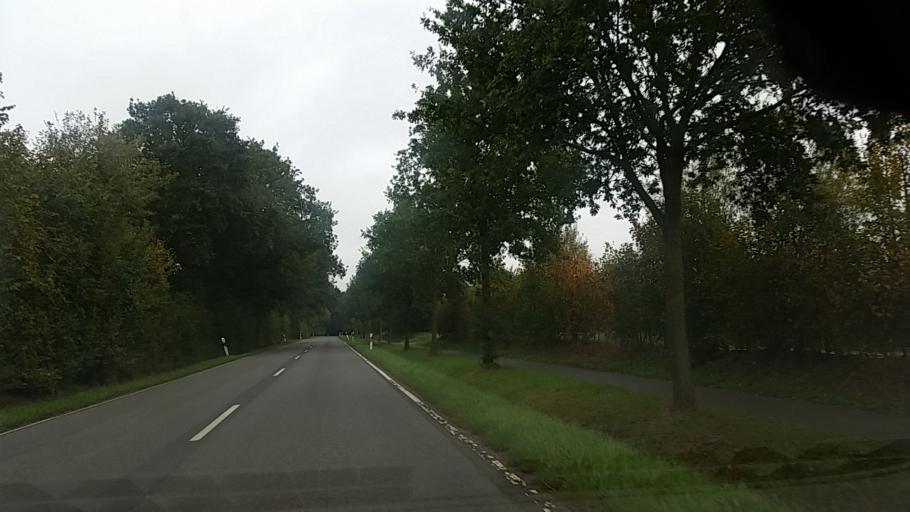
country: DE
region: Schleswig-Holstein
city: Schmalfeld
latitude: 53.8652
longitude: 9.9768
